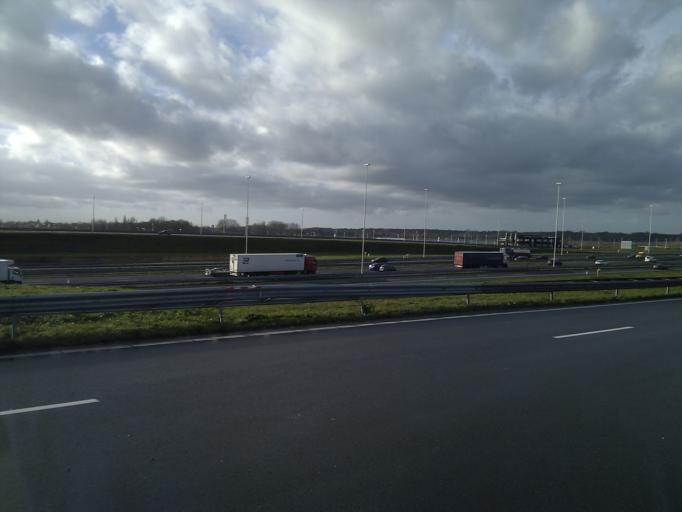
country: NL
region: Utrecht
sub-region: Stichtse Vecht
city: Maarssen
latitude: 52.1189
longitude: 5.0339
